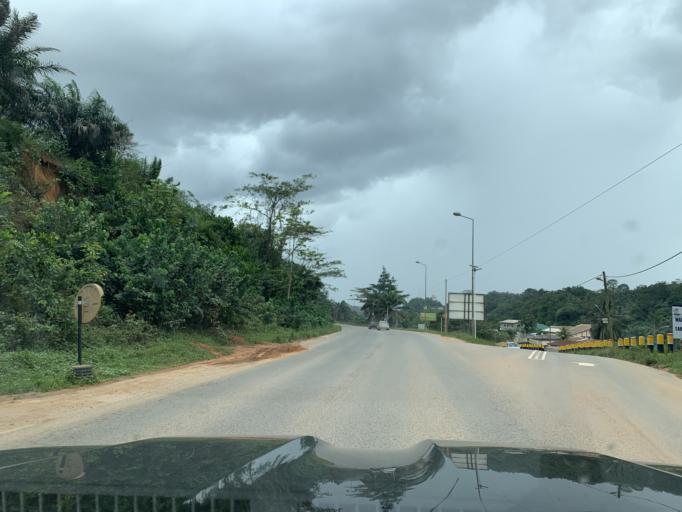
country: GH
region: Western
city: Tarkwa
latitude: 5.3217
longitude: -1.9852
